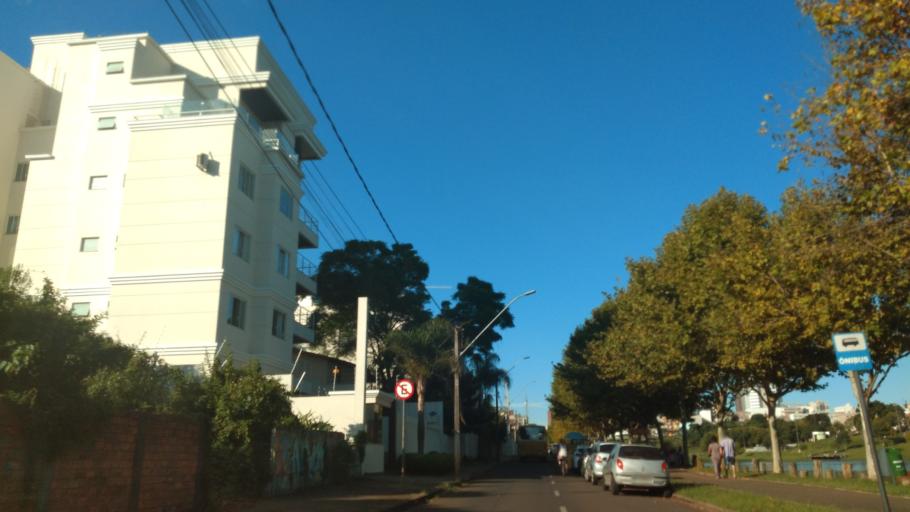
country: BR
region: Parana
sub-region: Guarapuava
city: Guarapuava
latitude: -25.4004
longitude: -51.4753
